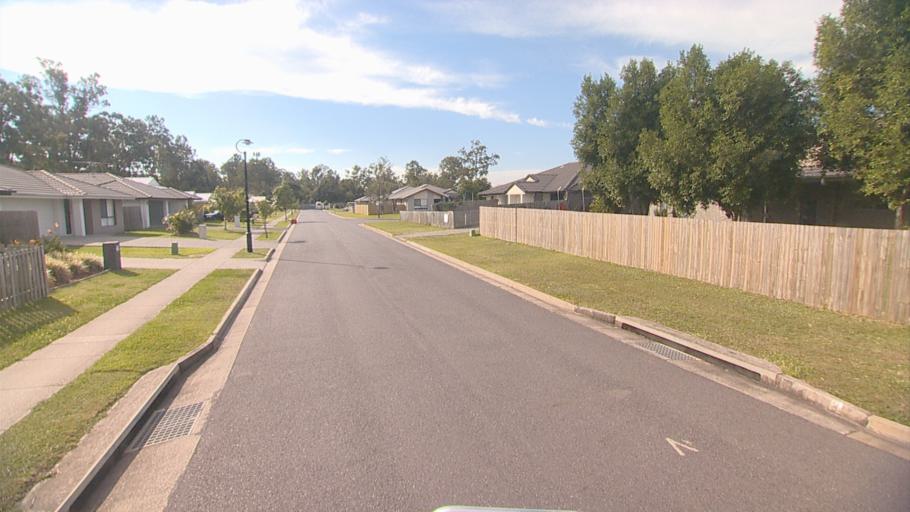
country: AU
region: Queensland
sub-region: Logan
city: Windaroo
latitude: -27.7587
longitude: 153.1863
